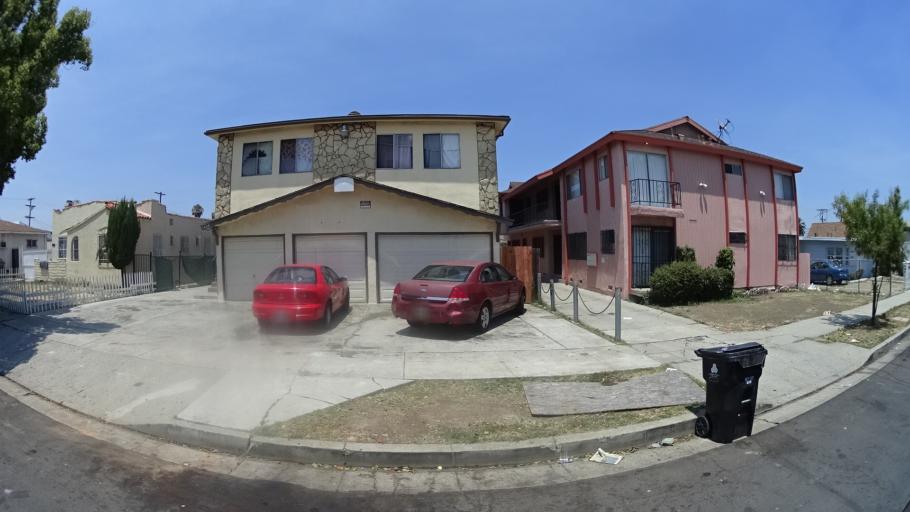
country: US
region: California
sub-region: Los Angeles County
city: Westmont
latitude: 33.9646
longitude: -118.3037
